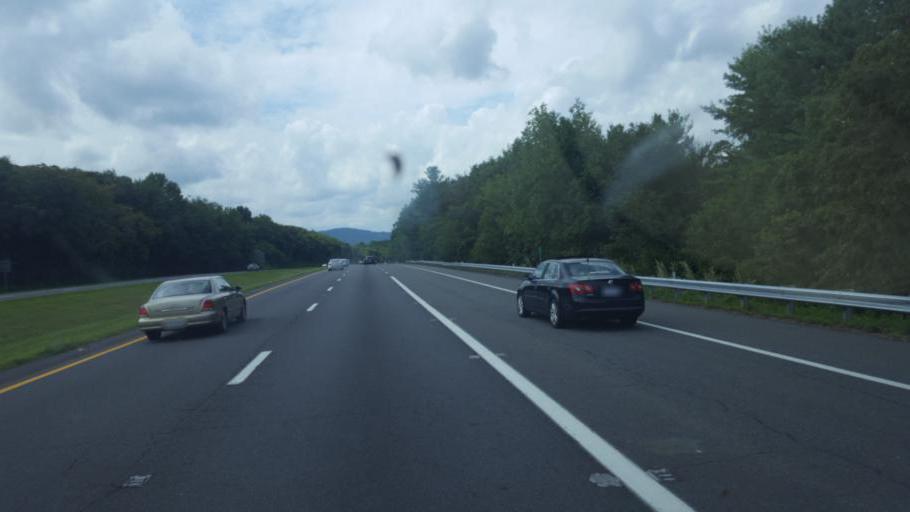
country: US
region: Virginia
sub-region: Fauquier County
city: Marshall
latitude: 38.8603
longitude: -77.8710
